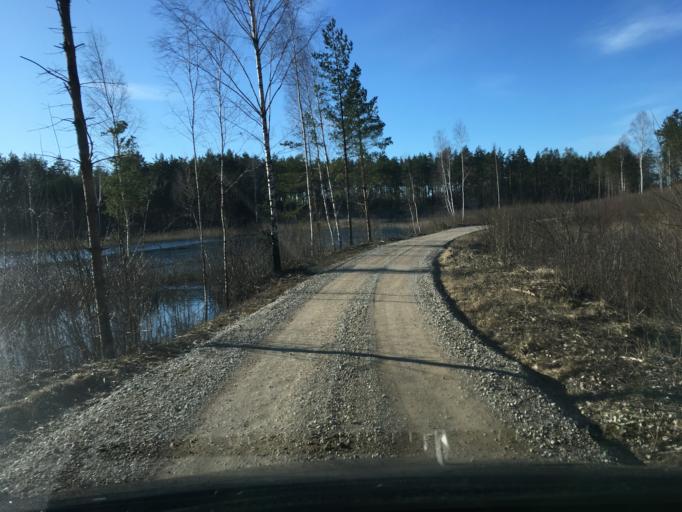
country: EE
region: Laeaene
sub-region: Lihula vald
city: Lihula
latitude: 58.5696
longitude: 23.6927
